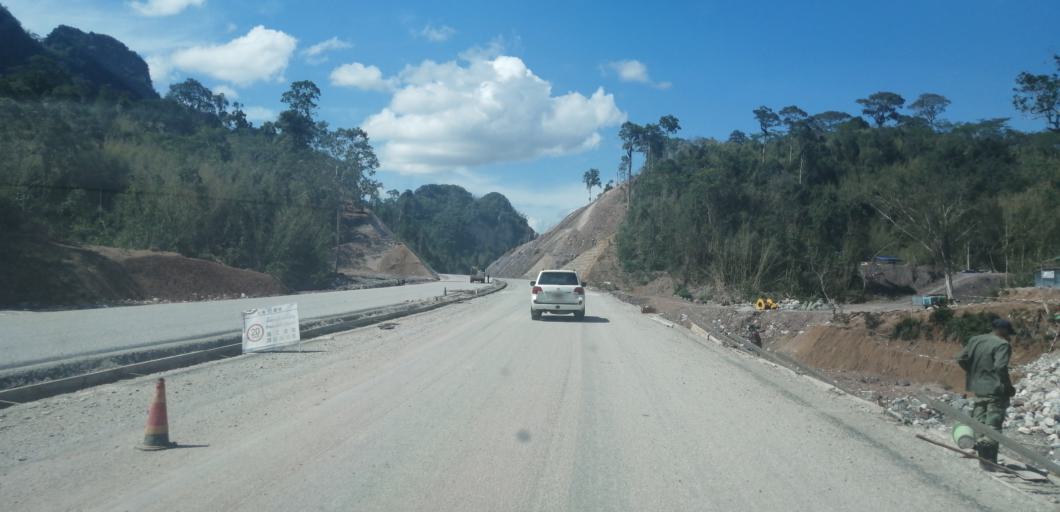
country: LA
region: Vientiane
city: Vangviang
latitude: 18.8580
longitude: 102.4214
